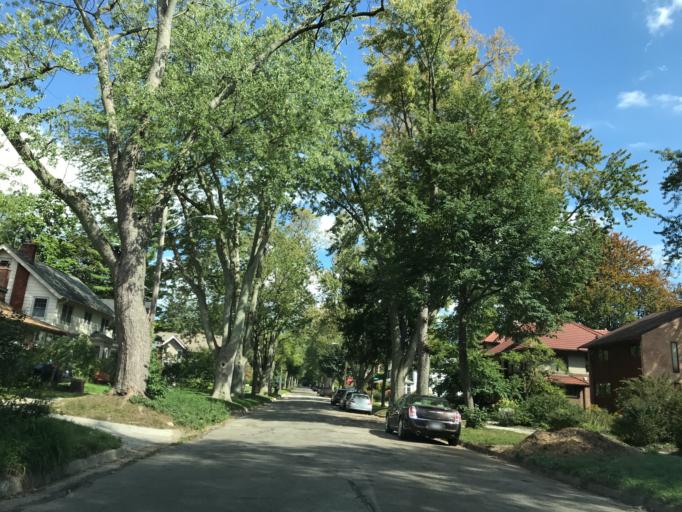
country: US
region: Michigan
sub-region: Washtenaw County
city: Ann Arbor
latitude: 42.2645
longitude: -83.7310
